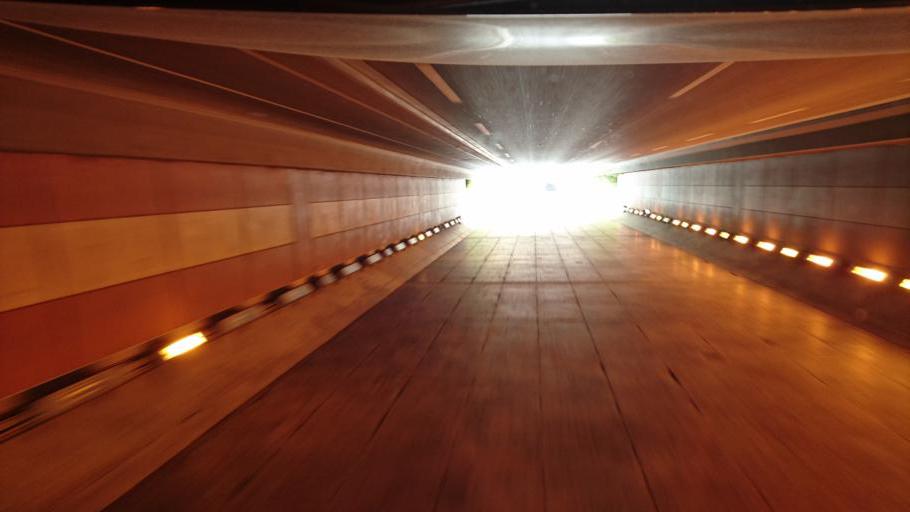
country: FR
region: Midi-Pyrenees
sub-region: Departement de la Haute-Garonne
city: Beauzelle
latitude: 43.6449
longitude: 1.3578
